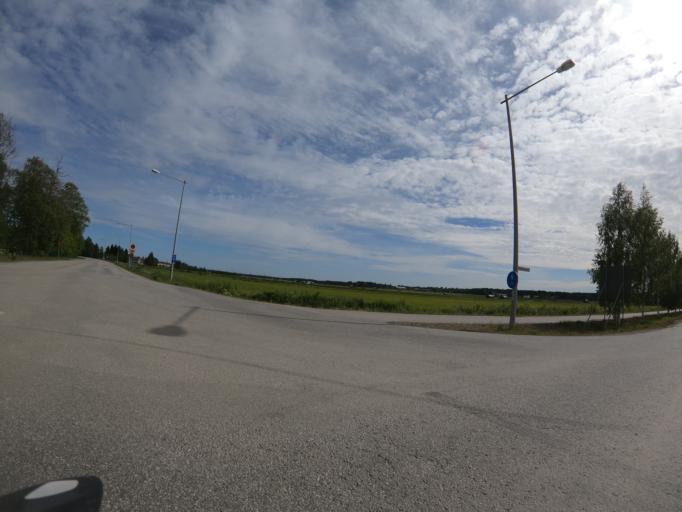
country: SE
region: Vaesterbotten
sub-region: Umea Kommun
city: Umea
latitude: 63.8223
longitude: 20.2400
